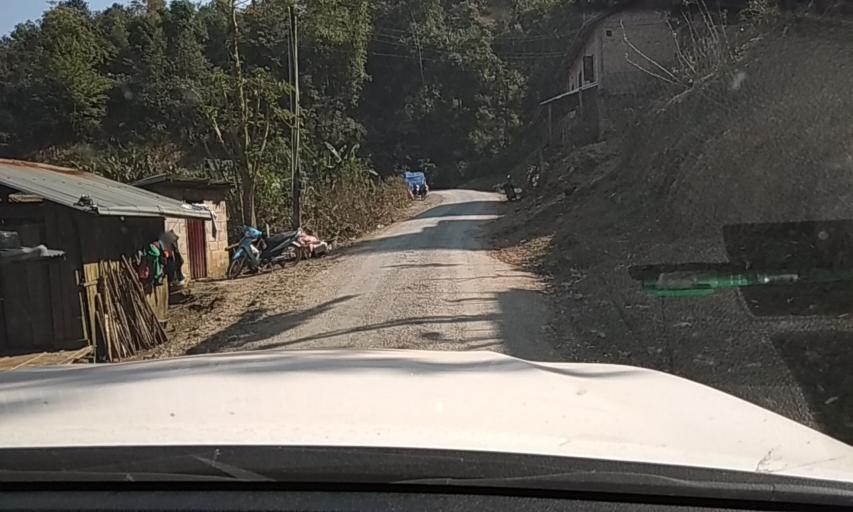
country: LA
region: Phongsali
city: Phongsali
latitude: 21.6615
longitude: 102.0901
